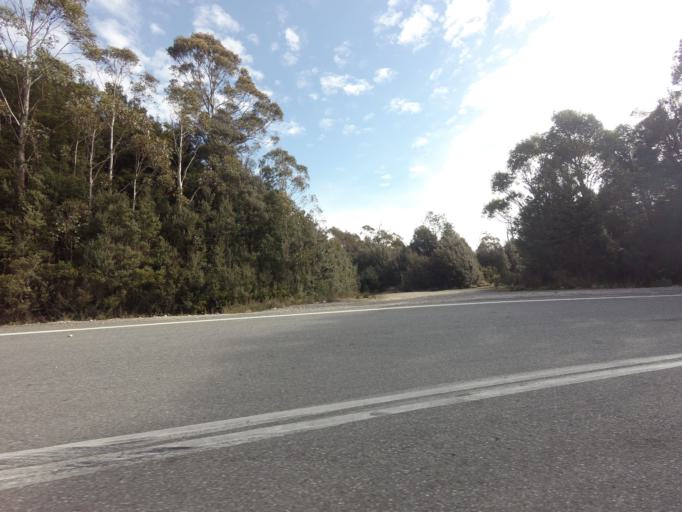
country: AU
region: Tasmania
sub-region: Meander Valley
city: Deloraine
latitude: -41.7036
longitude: 146.7247
